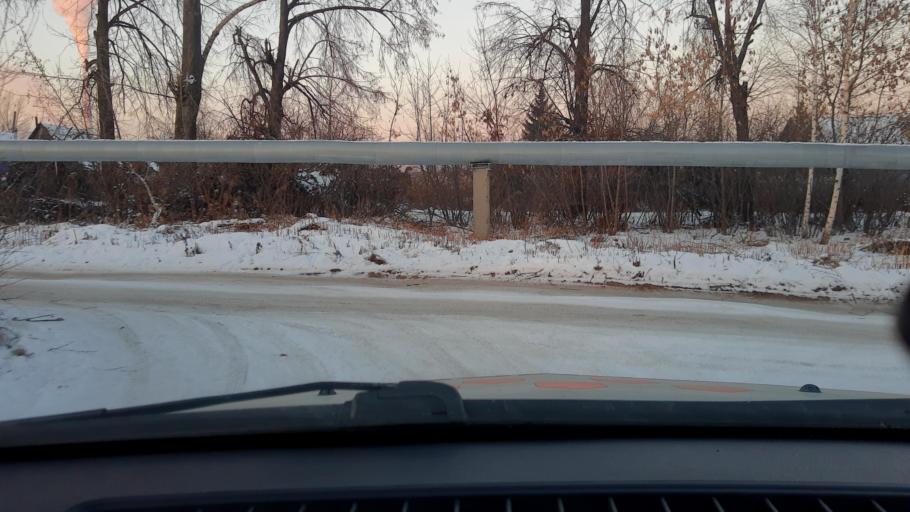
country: RU
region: Bashkortostan
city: Ufa
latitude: 54.8370
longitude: 56.1349
